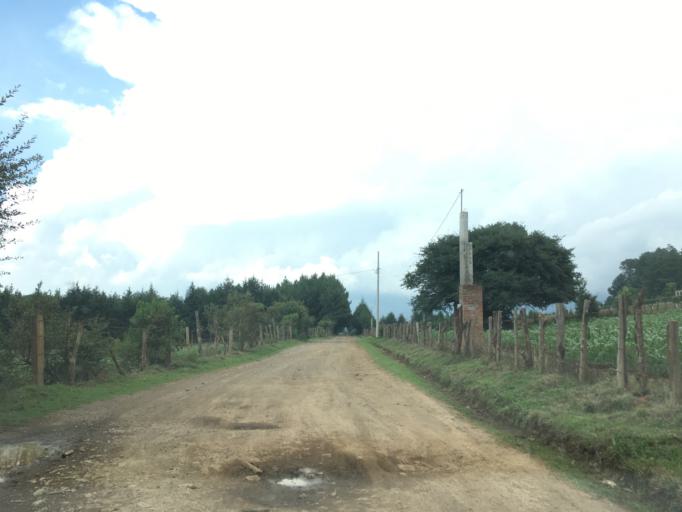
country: MX
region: Michoacan
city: Acuitzio del Canje
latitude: 19.4957
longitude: -101.2324
